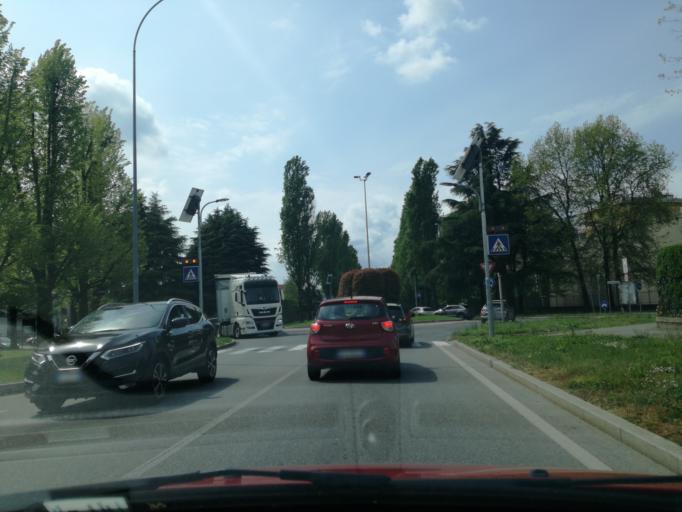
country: IT
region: Lombardy
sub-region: Provincia di Monza e Brianza
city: Carate Brianza
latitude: 45.6718
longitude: 9.2351
